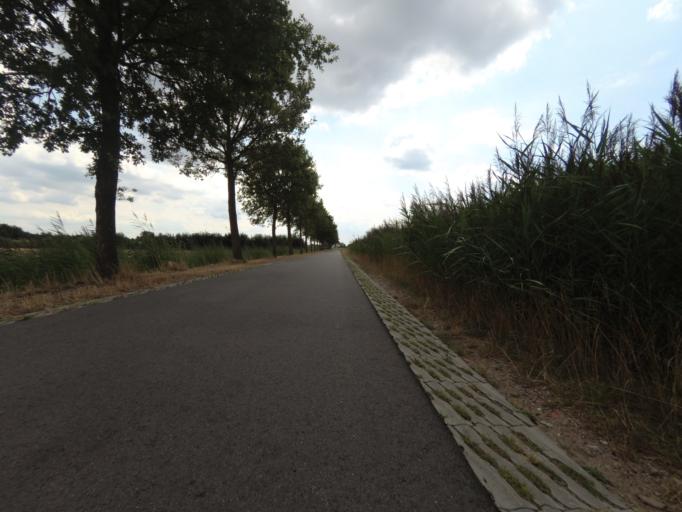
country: NL
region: Gelderland
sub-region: Berkelland
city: Eibergen
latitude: 52.1449
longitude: 6.6741
